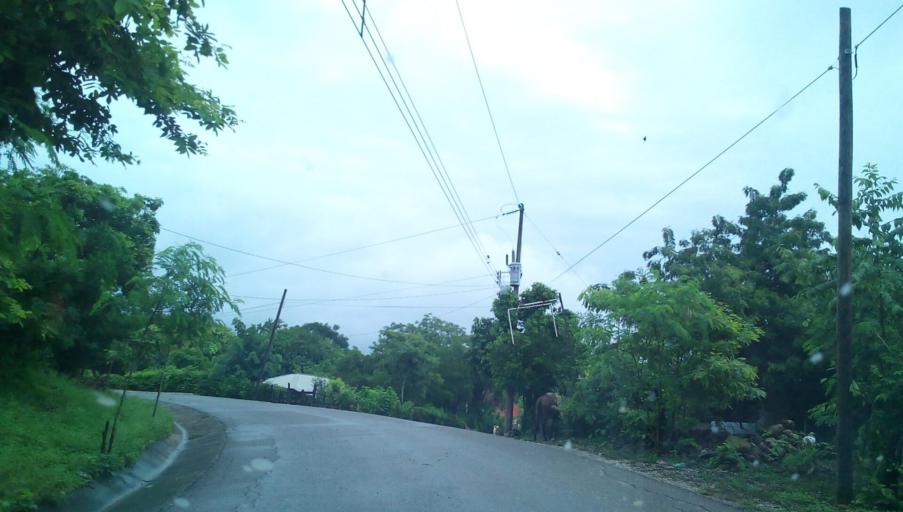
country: MX
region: Veracruz
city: Tempoal de Sanchez
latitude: 21.4632
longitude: -98.4218
